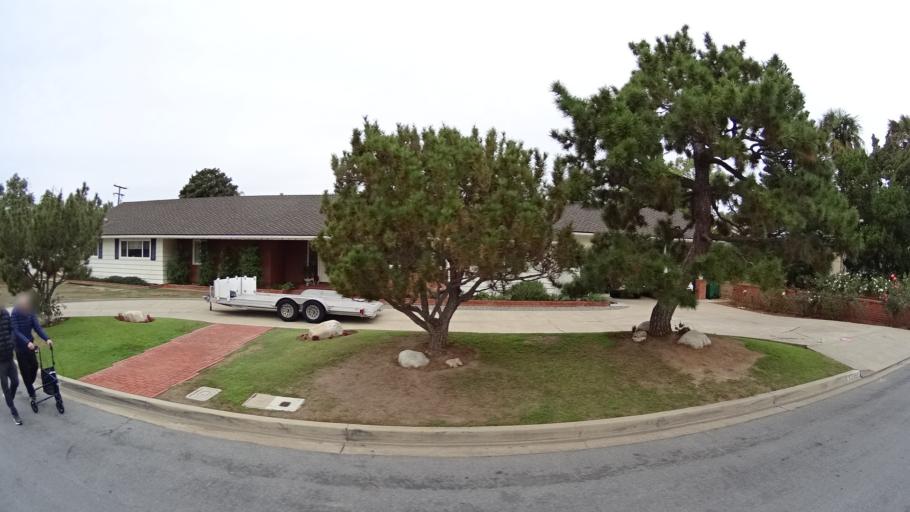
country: US
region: California
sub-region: Orange County
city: North Tustin
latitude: 33.7532
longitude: -117.7911
